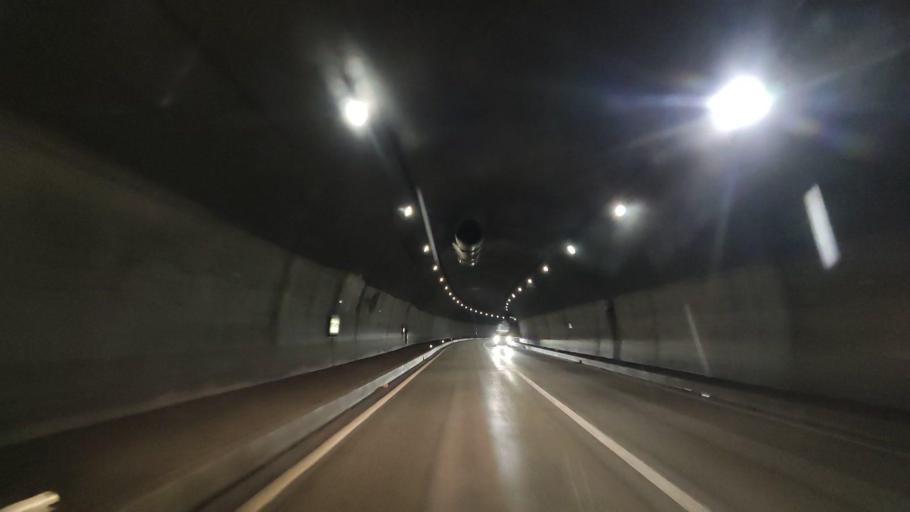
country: JP
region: Nagano
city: Omachi
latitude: 36.5488
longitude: 137.8441
